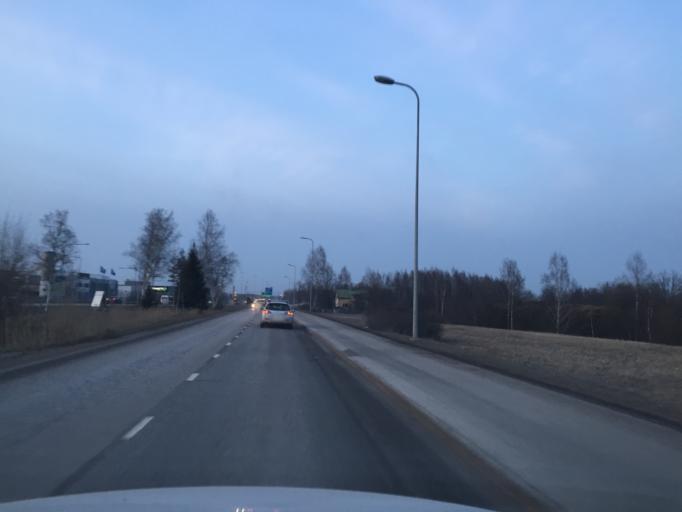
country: FI
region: Uusimaa
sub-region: Helsinki
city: Vantaa
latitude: 60.2722
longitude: 24.9758
